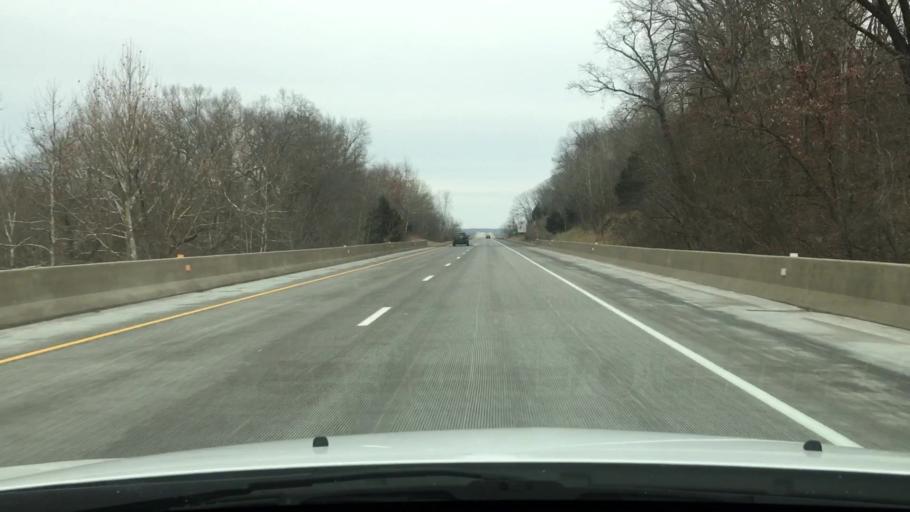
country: US
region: Illinois
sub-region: Pike County
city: Griggsville
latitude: 39.6834
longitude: -90.6497
